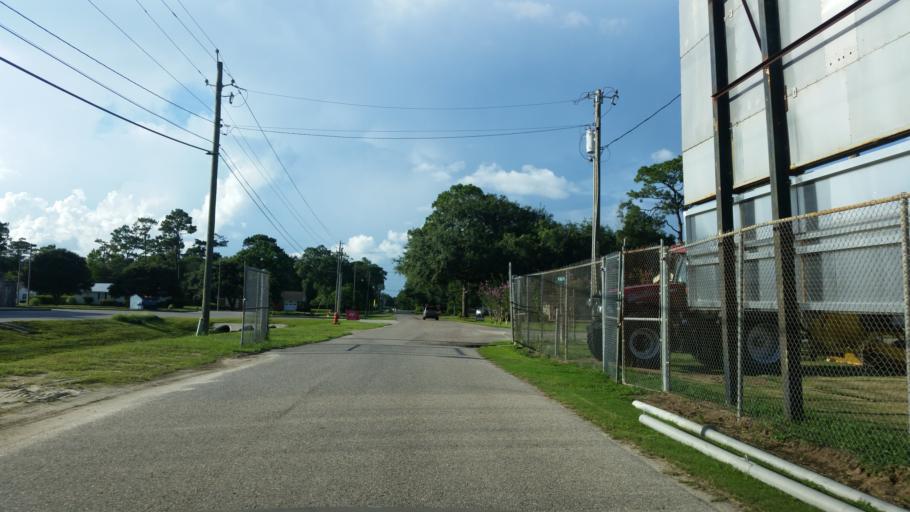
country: US
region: Alabama
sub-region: Baldwin County
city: Foley
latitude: 30.4094
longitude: -87.6895
